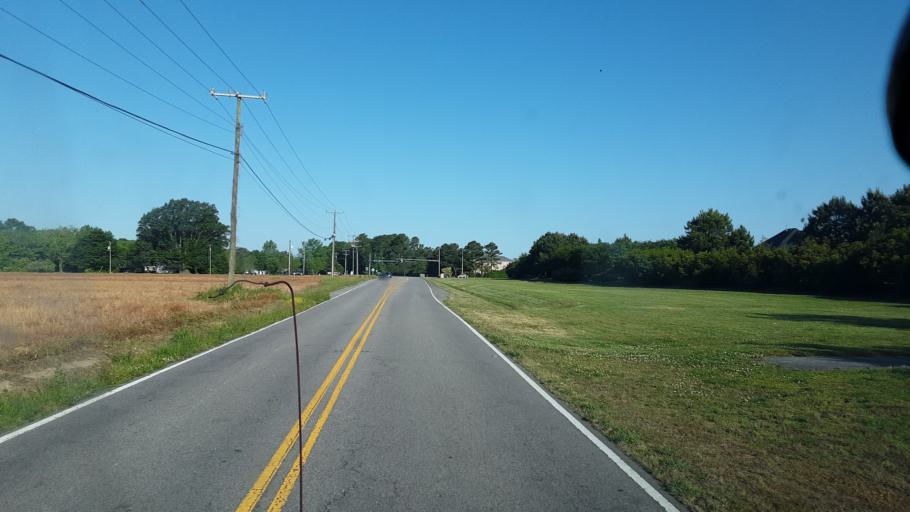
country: US
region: Virginia
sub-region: City of Virginia Beach
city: Virginia Beach
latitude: 36.7213
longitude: -76.0486
